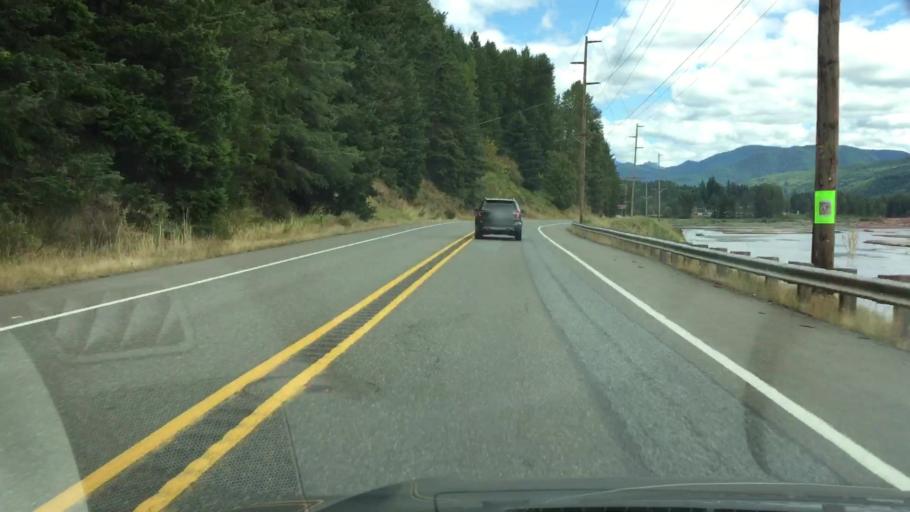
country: US
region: Washington
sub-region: Pierce County
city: Eatonville
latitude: 46.7711
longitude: -122.2106
